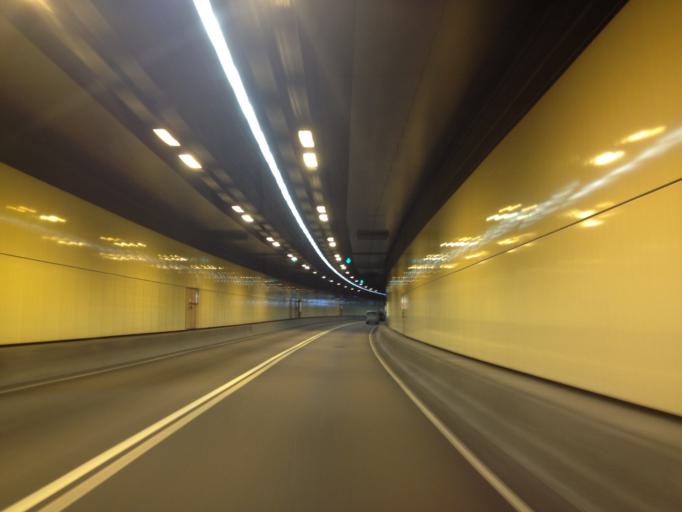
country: HK
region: Sha Tin
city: Sha Tin
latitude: 22.3711
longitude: 114.1745
